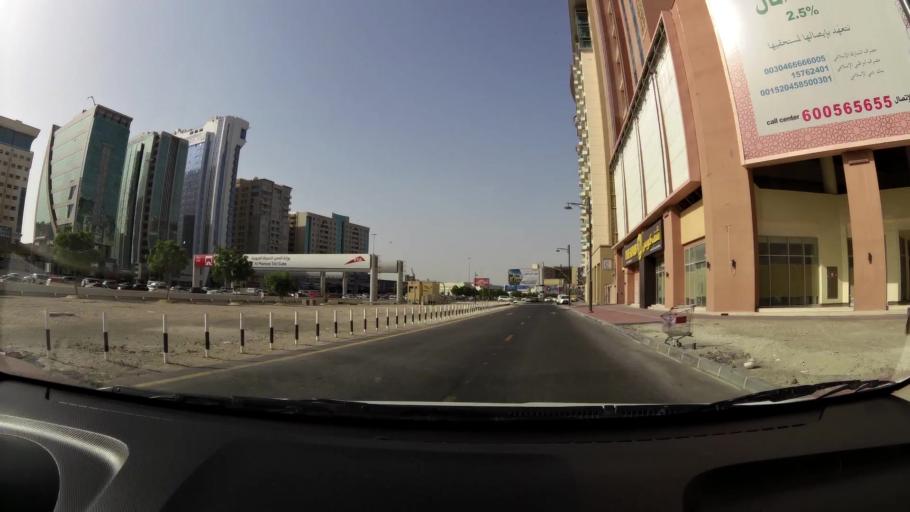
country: AE
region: Ash Shariqah
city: Sharjah
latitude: 25.2870
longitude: 55.3586
